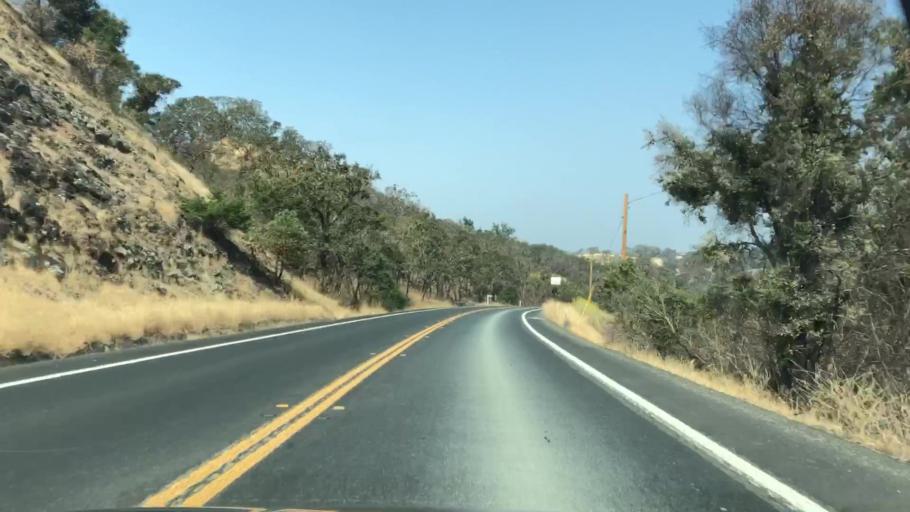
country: US
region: California
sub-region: Sonoma County
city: Larkfield-Wikiup
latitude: 38.5561
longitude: -122.6841
